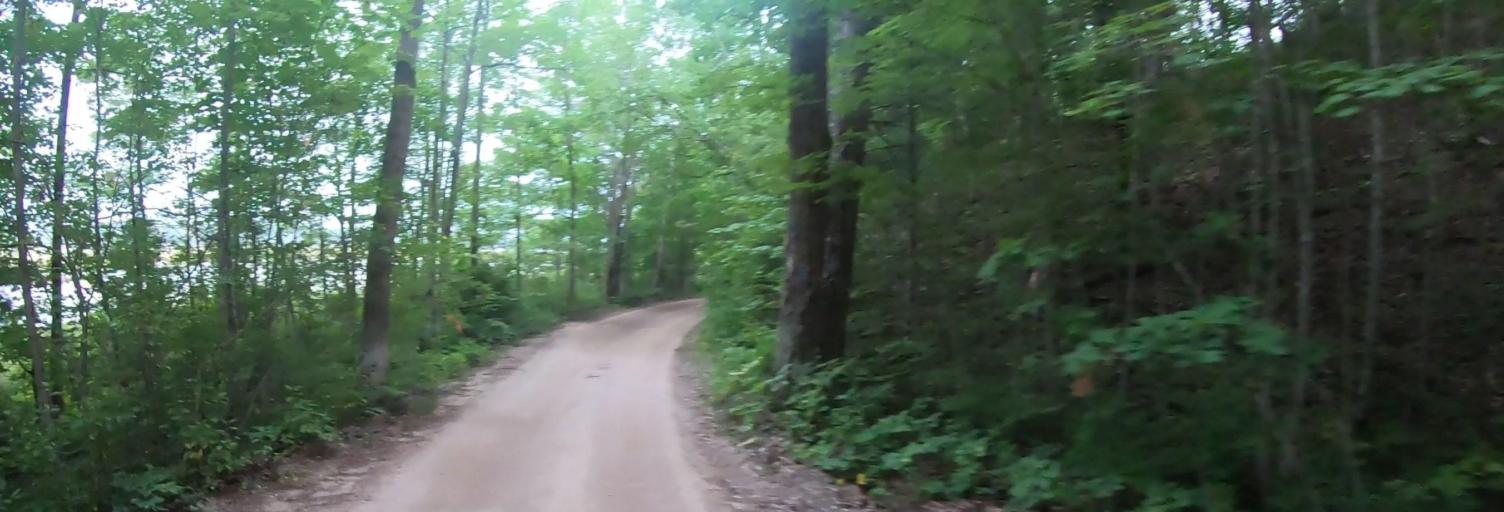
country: US
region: Michigan
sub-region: Mackinac County
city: Saint Ignace
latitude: 45.7615
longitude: -84.7670
